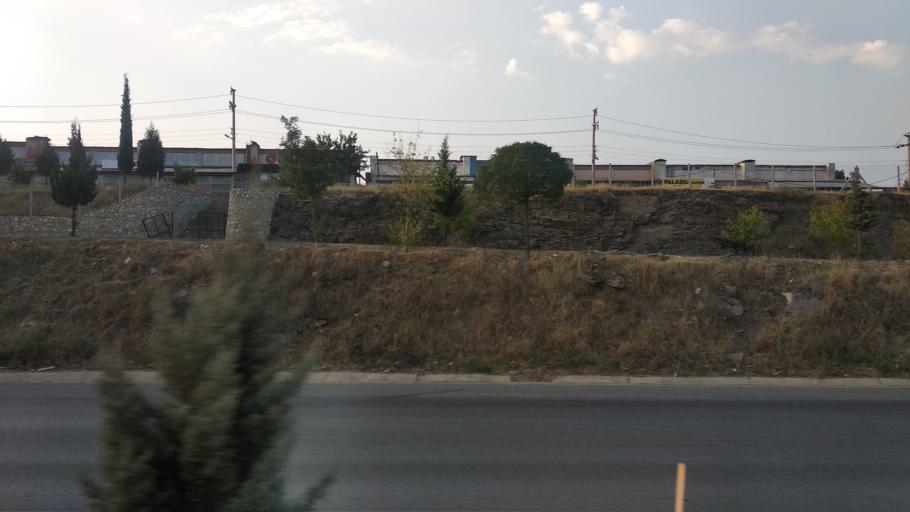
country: TR
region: Manisa
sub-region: Kula
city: Kula
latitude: 38.5466
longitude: 28.6682
